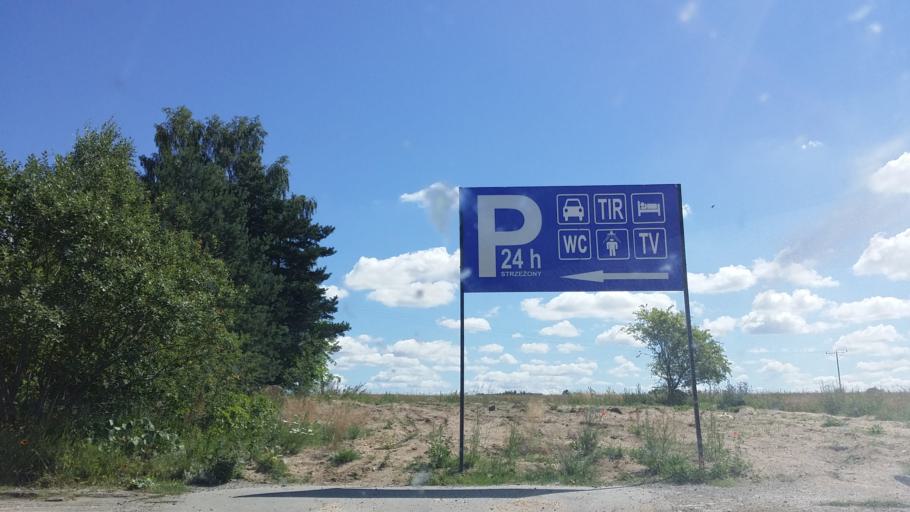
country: PL
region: West Pomeranian Voivodeship
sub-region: Powiat swidwinski
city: Swidwin
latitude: 53.7847
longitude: 15.7849
